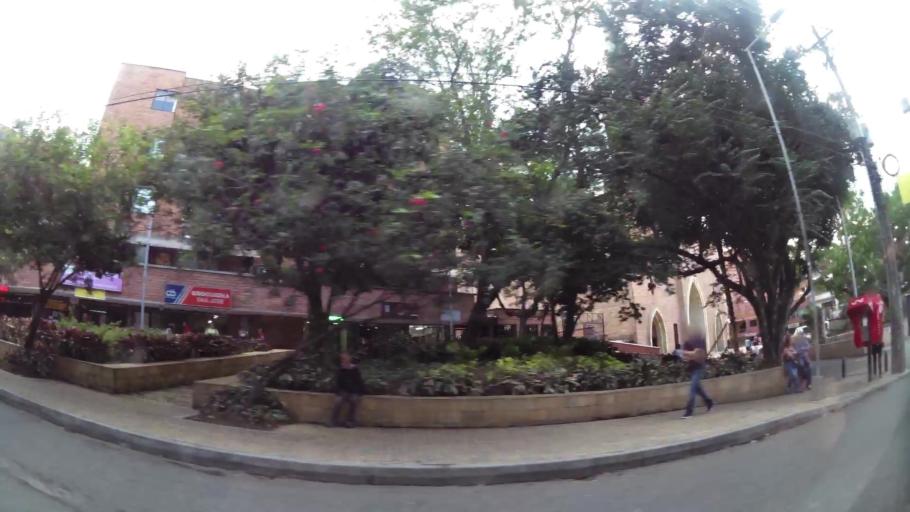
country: CO
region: Antioquia
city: Envigado
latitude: 6.1618
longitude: -75.5822
